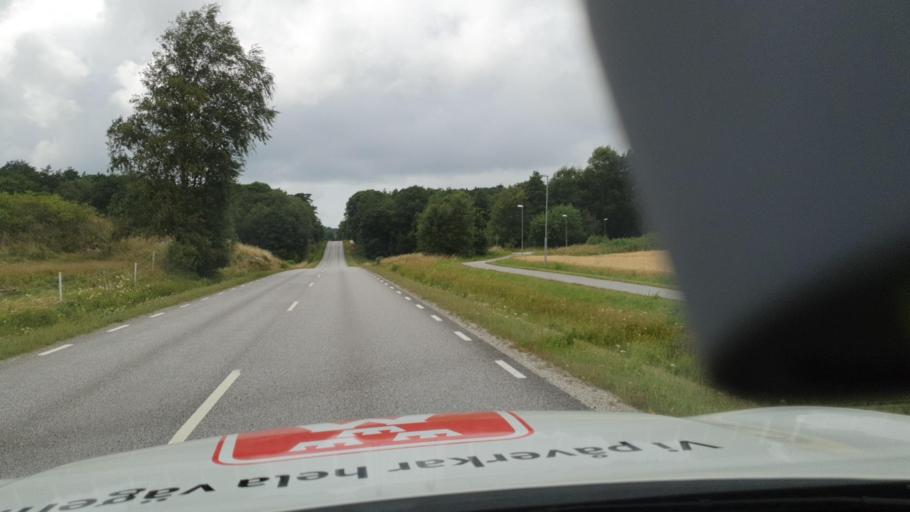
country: SE
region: Vaestra Goetaland
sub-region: Tanums Kommun
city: Tanumshede
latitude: 58.7222
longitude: 11.3129
